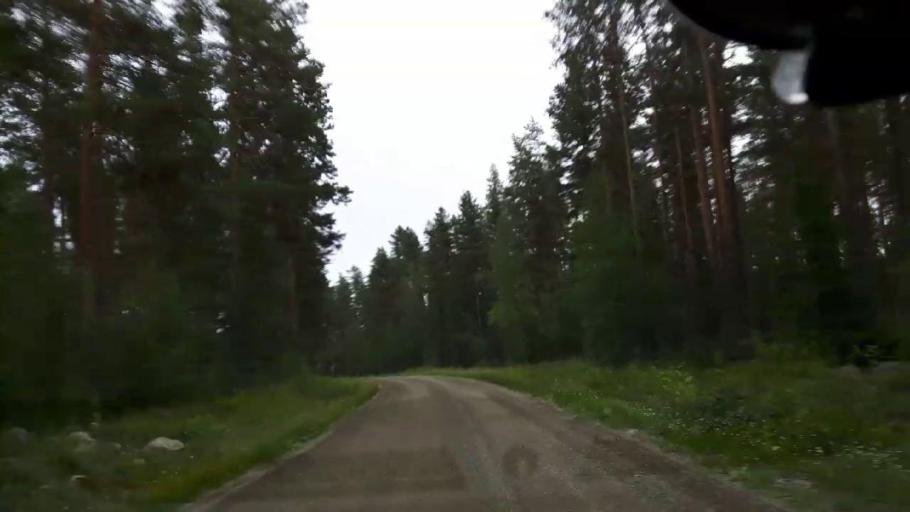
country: SE
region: Jaemtland
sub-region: Braecke Kommun
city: Braecke
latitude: 62.9331
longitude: 15.4731
